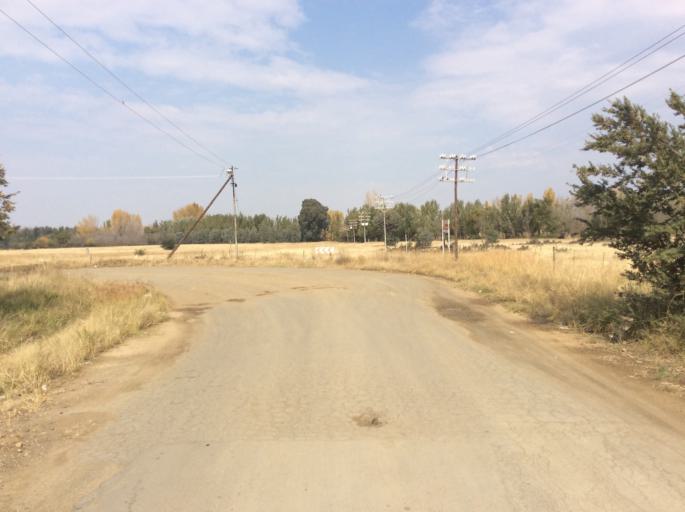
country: LS
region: Mafeteng
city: Mafeteng
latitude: -29.7322
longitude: 27.0386
